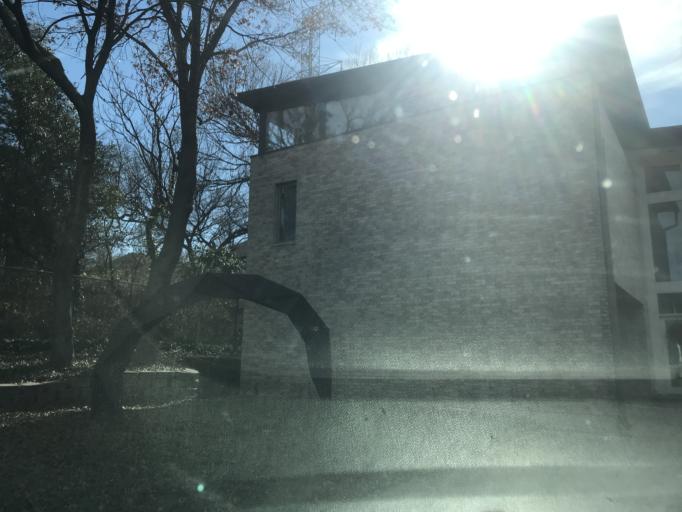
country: US
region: Texas
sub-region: Dallas County
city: Highland Park
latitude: 32.8214
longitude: -96.7937
